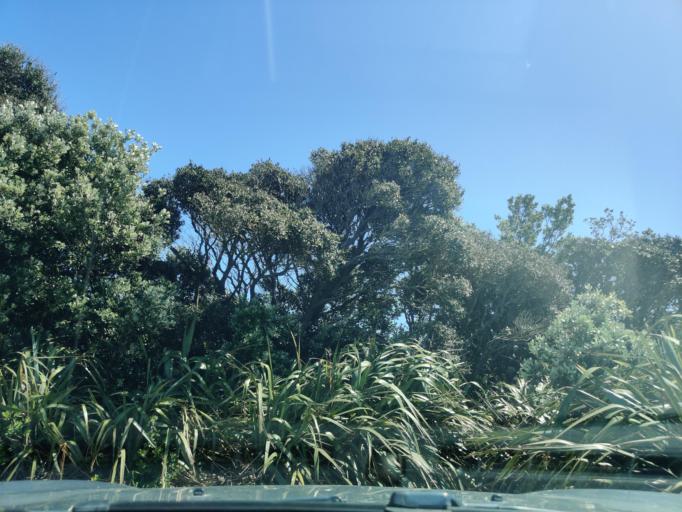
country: NZ
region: Taranaki
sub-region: South Taranaki District
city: Hawera
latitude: -39.6052
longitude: 174.2419
